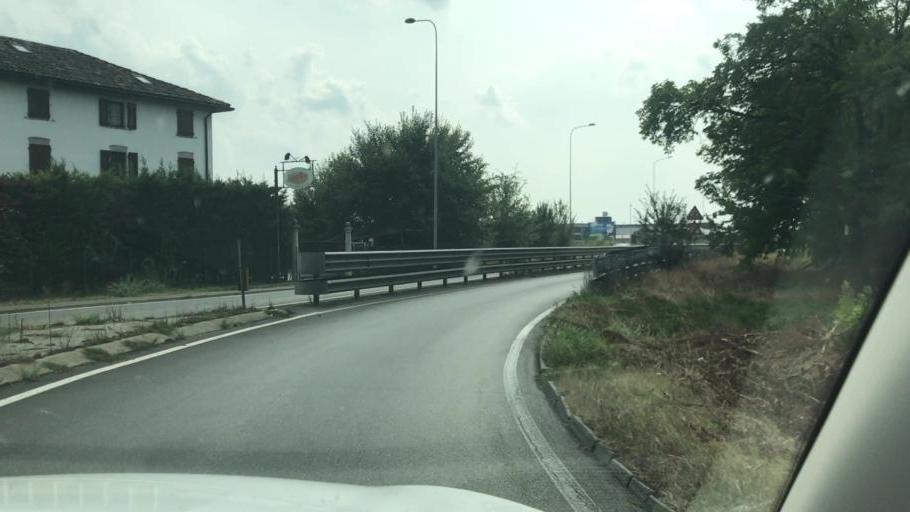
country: IT
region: Emilia-Romagna
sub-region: Provincia di Parma
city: Baganzola
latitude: 44.8477
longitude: 10.3412
